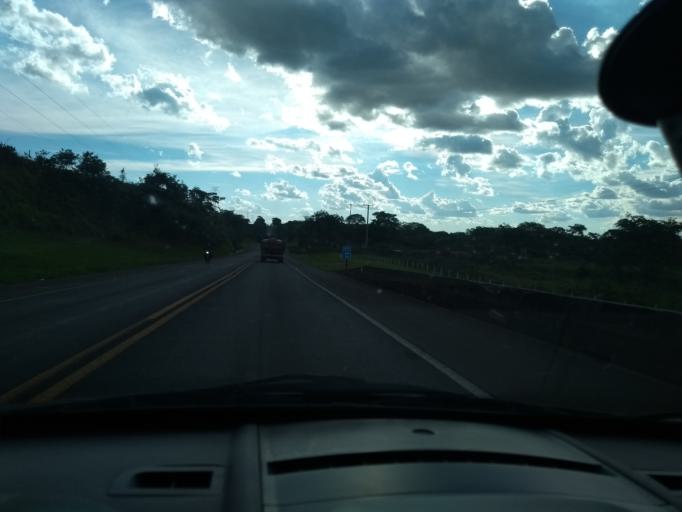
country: BR
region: Sao Paulo
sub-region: Casa Branca
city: Casa Branca
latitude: -21.7983
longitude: -47.0810
